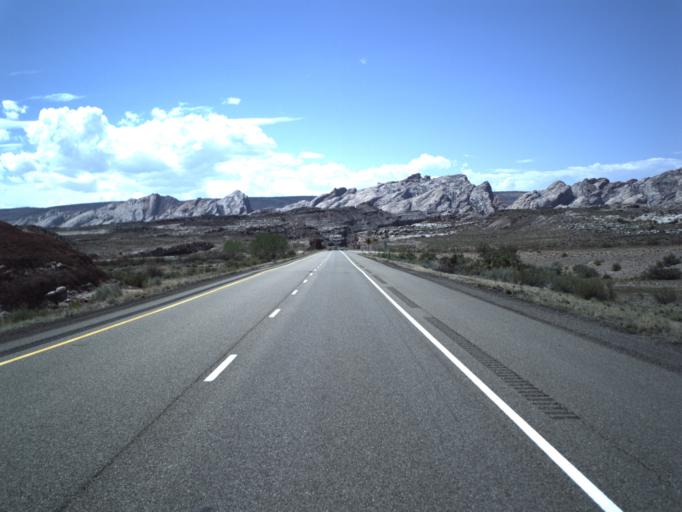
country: US
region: Utah
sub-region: Carbon County
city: East Carbon City
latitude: 38.9232
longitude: -110.3781
